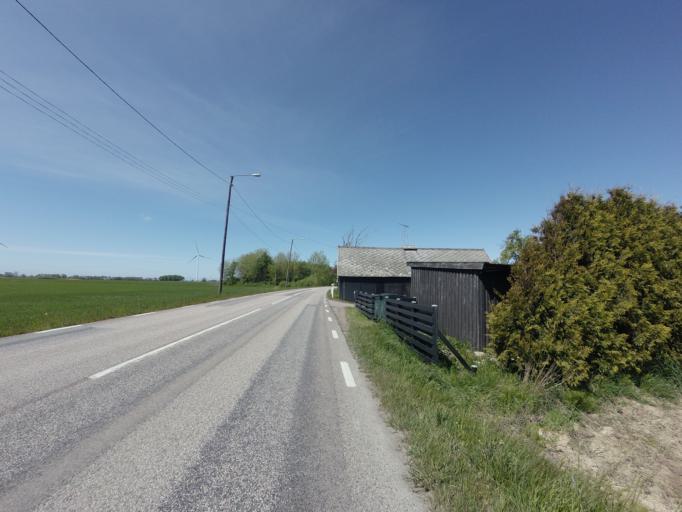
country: SE
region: Skane
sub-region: Helsingborg
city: Odakra
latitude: 56.1472
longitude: 12.6795
